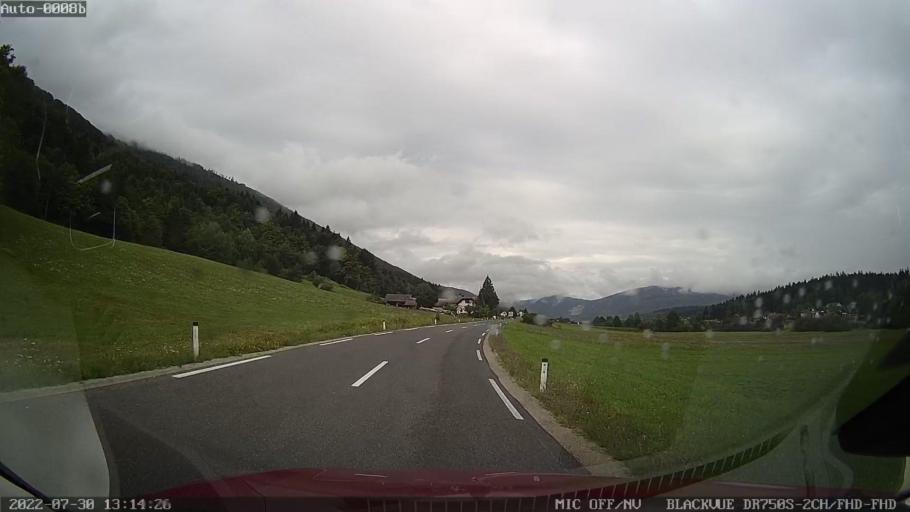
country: SI
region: Dolenjske Toplice
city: Dolenjske Toplice
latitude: 45.7310
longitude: 15.0476
